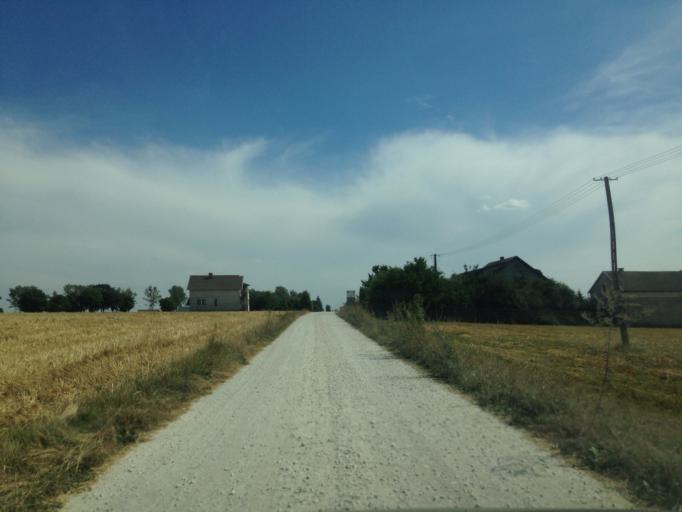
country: PL
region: Kujawsko-Pomorskie
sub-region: Powiat brodnicki
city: Bartniczka
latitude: 53.2311
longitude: 19.5918
